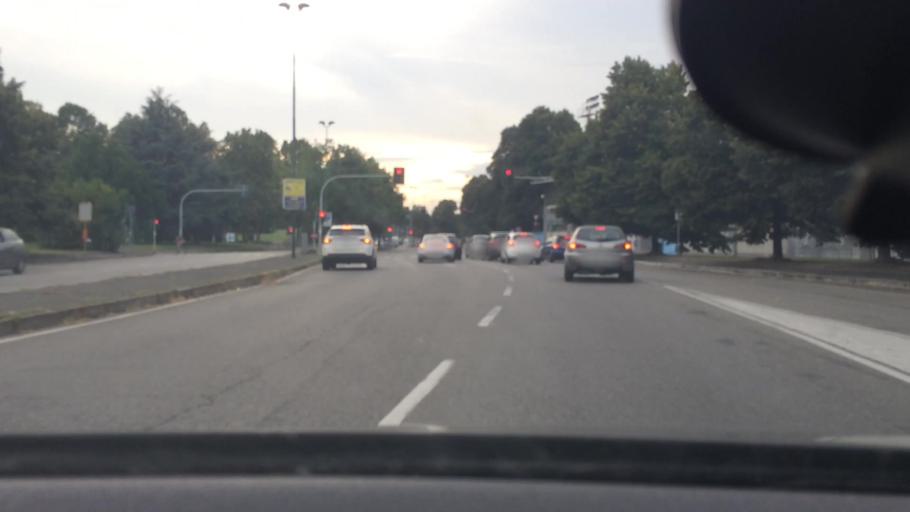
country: IT
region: Lombardy
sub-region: Citta metropolitana di Milano
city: Sesto San Giovanni
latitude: 45.5322
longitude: 9.2197
